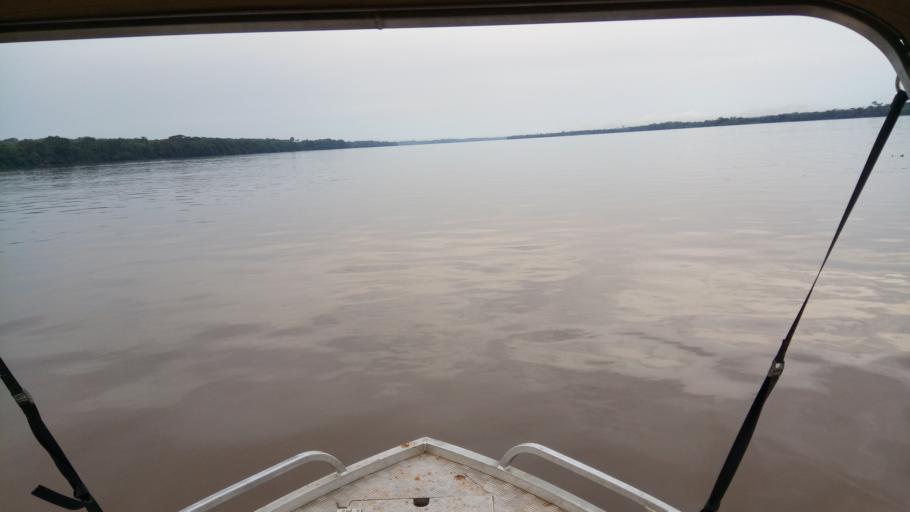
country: CD
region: Eastern Province
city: Kisangani
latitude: 0.5736
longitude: 24.8388
